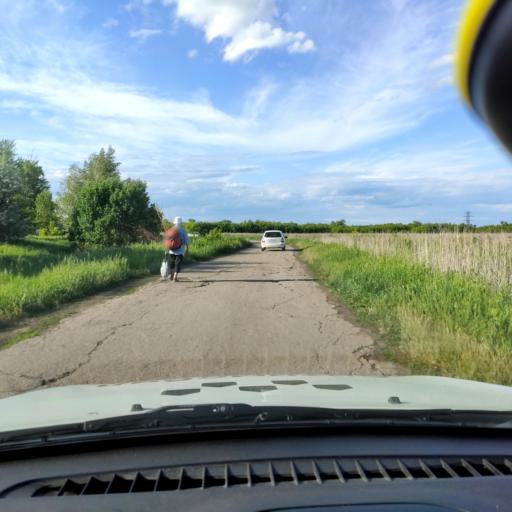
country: RU
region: Samara
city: Tol'yatti
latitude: 53.5949
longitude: 49.4571
